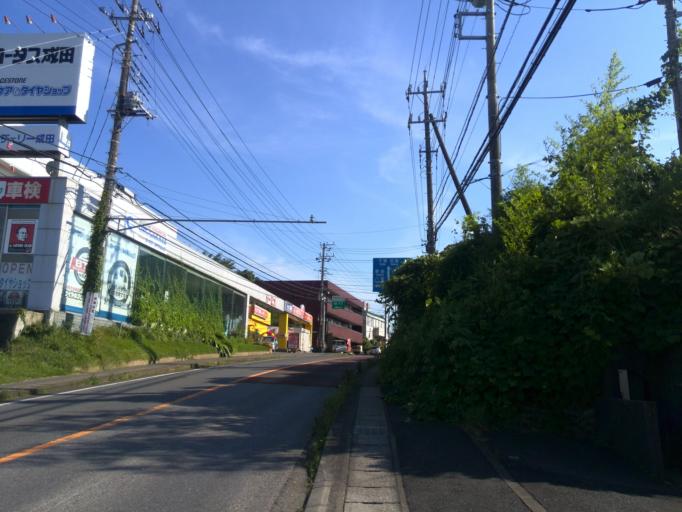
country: JP
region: Chiba
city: Narita
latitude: 35.7562
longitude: 140.3038
